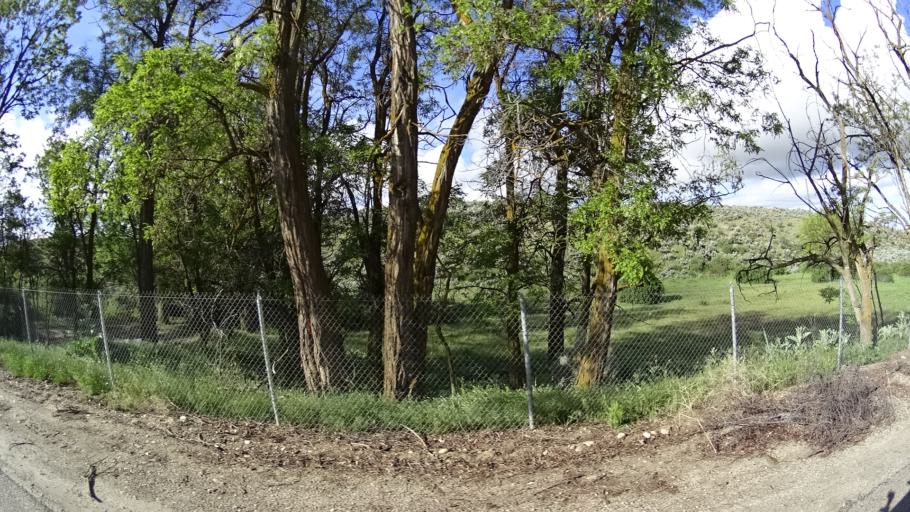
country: US
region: Idaho
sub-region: Ada County
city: Garden City
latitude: 43.6986
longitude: -116.2630
